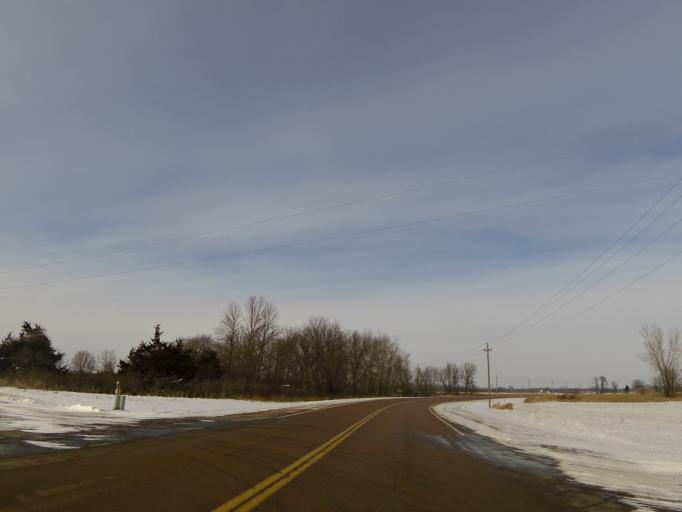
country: US
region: Minnesota
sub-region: McLeod County
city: Lester Prairie
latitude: 44.8913
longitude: -93.9708
